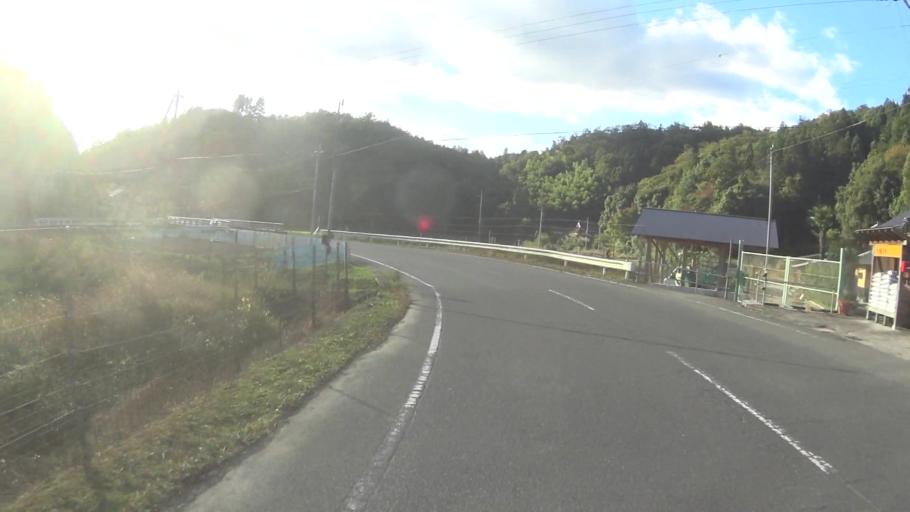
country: JP
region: Kyoto
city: Miyazu
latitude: 35.4629
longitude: 135.2406
